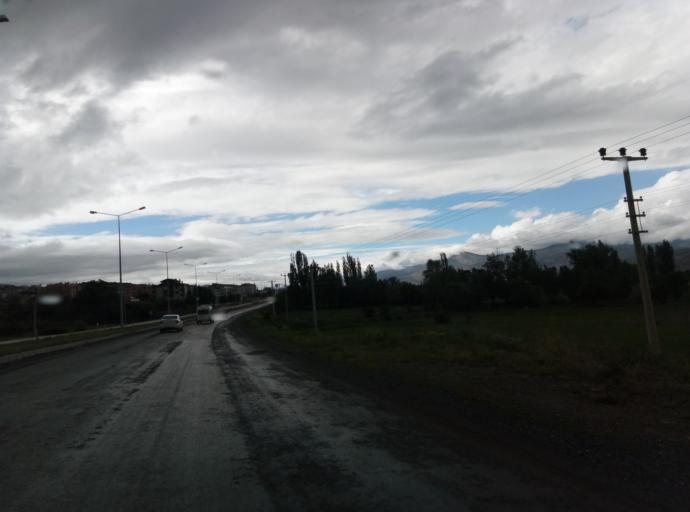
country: TR
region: Sivas
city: Susehri
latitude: 40.1696
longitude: 38.0944
